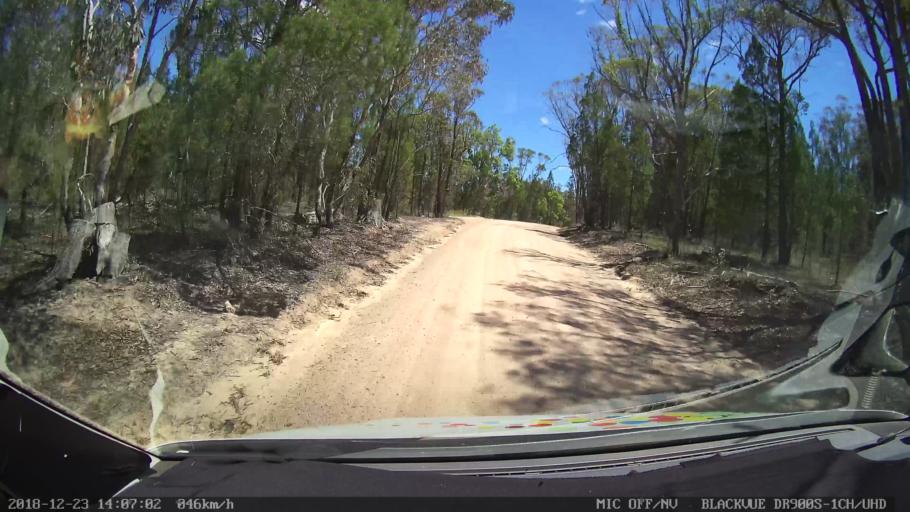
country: AU
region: New South Wales
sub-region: Tamworth Municipality
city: Manilla
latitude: -30.6334
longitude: 151.0734
